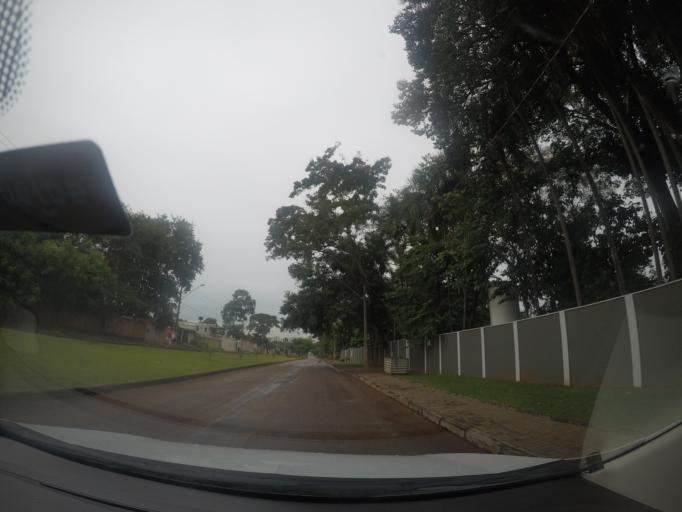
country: BR
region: Goias
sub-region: Goiania
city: Goiania
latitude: -16.6247
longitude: -49.2342
